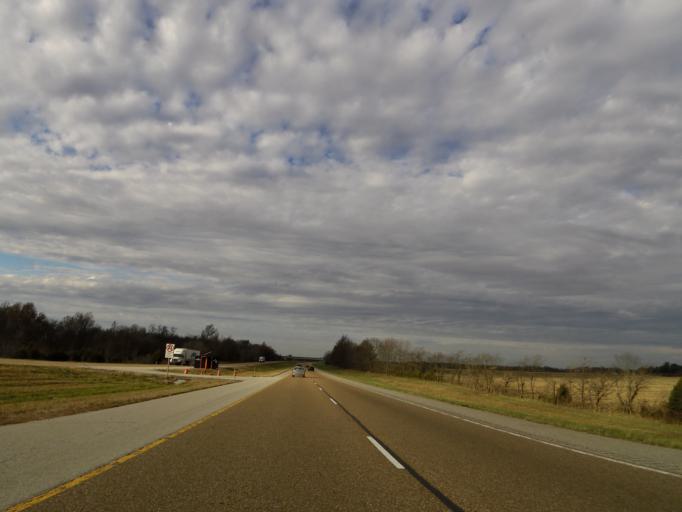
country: US
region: Illinois
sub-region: Clinton County
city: Wamac
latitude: 38.3899
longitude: -89.1832
